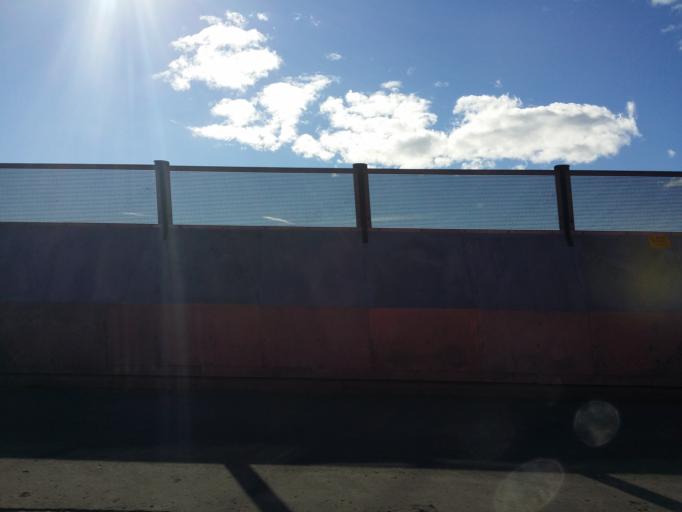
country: NO
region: Oslo
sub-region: Oslo
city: Oslo
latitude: 59.8953
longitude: 10.7572
